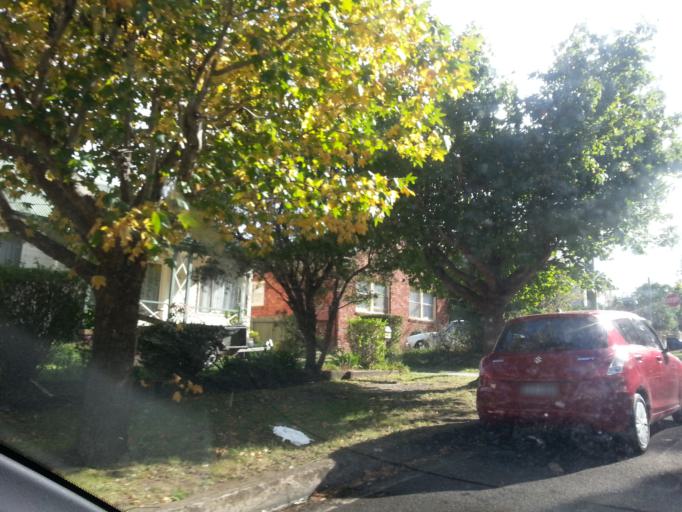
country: AU
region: New South Wales
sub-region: Wollongong
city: Gwynneville
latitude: -34.4194
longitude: 150.8819
